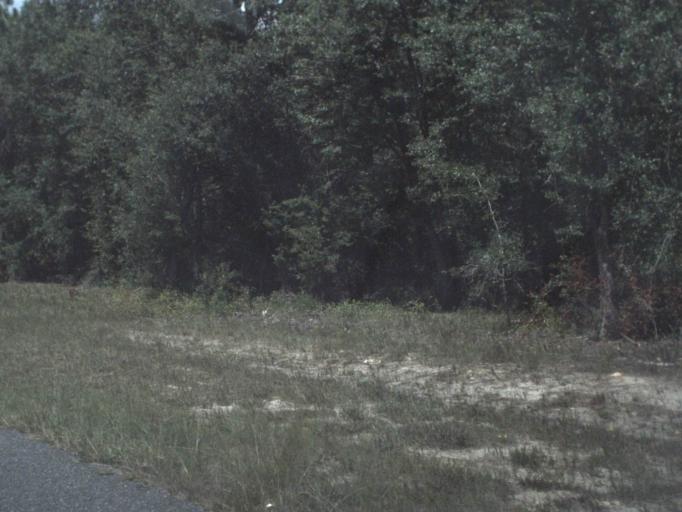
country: US
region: Florida
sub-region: Alachua County
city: High Springs
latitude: 29.7612
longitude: -82.7406
